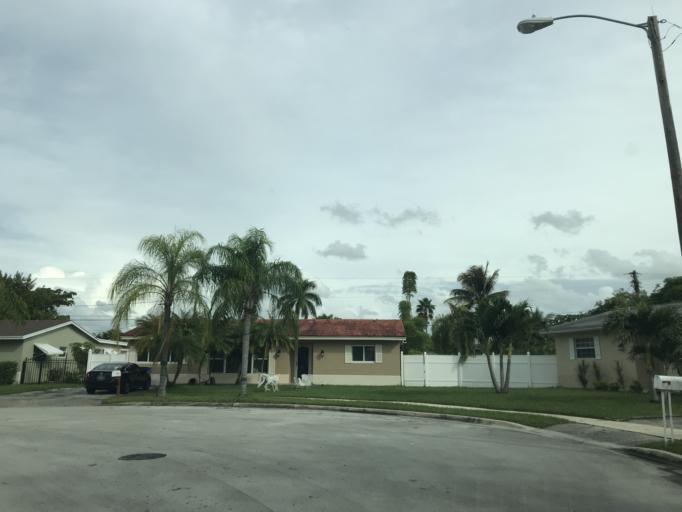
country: US
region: Florida
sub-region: Broward County
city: Margate
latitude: 26.2546
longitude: -80.2113
